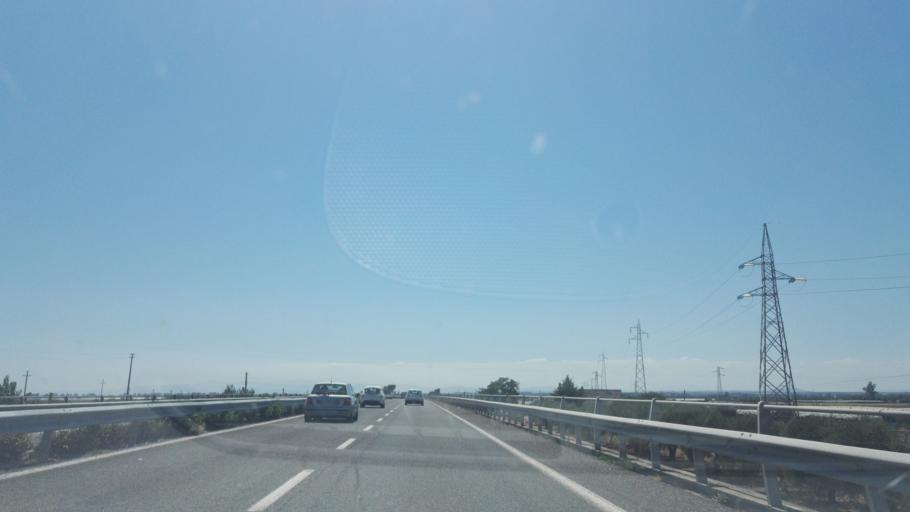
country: IT
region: Apulia
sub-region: Provincia di Taranto
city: Marina di Ginosa
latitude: 40.4435
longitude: 16.8502
